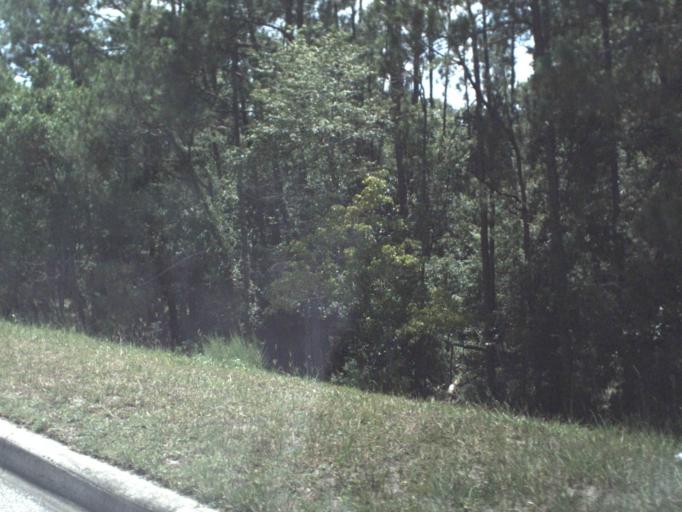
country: US
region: Florida
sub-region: Alachua County
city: Waldo
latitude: 29.7888
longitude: -82.1676
